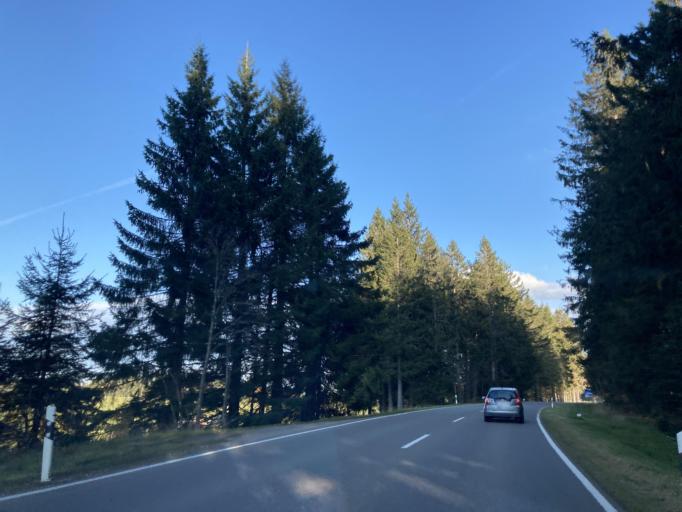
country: DE
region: Baden-Wuerttemberg
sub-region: Freiburg Region
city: Gutenbach
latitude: 47.9939
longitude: 8.1744
